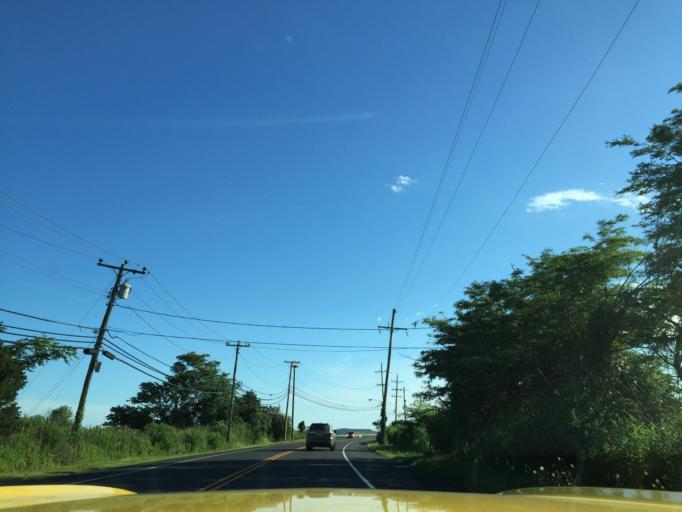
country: US
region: New York
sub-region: Suffolk County
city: Greenport
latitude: 41.1385
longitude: -72.3190
